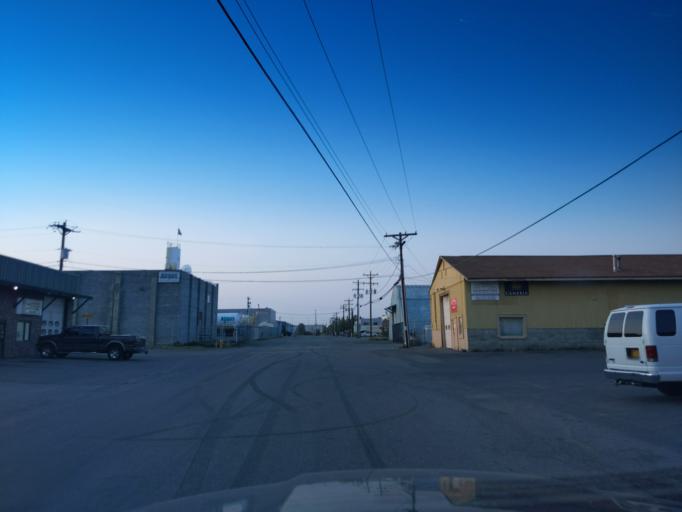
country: US
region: Alaska
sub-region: Anchorage Municipality
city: Anchorage
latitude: 61.1605
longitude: -149.8958
